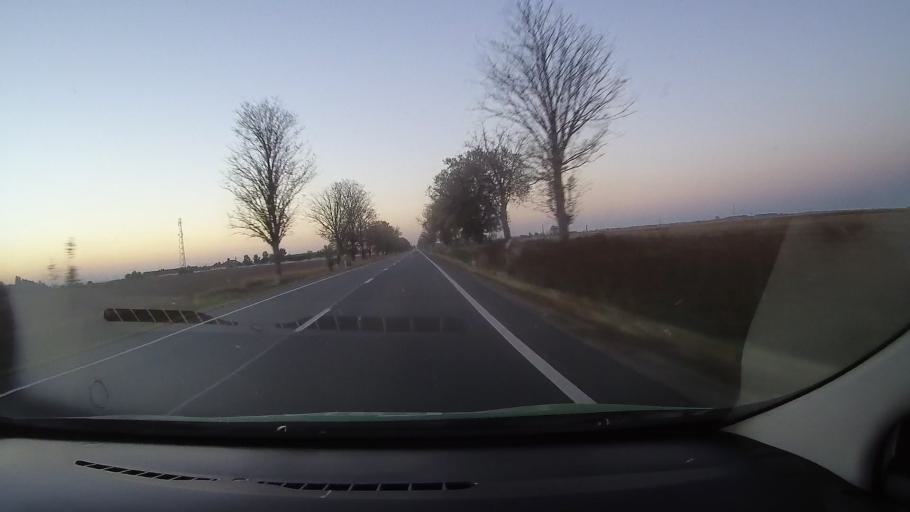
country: RO
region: Bihor
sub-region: Comuna Valea lui Mihai
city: Valea lui Mihai
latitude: 47.4966
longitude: 22.1509
